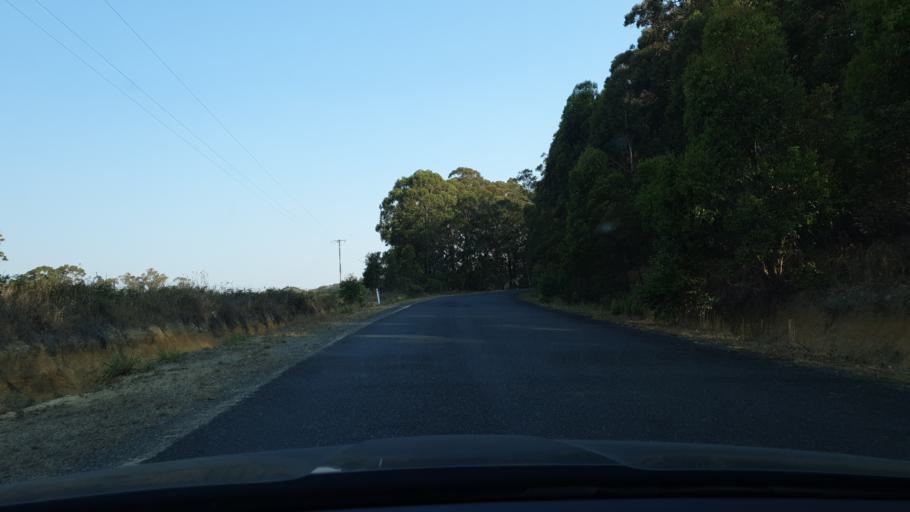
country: AU
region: New South Wales
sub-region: Tenterfield Municipality
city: Carrolls Creek
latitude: -28.6920
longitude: 152.0894
